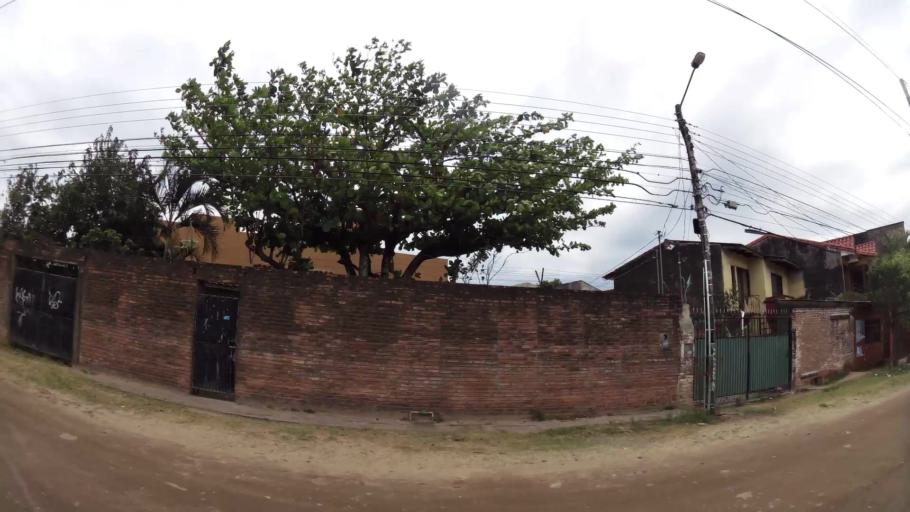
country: BO
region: Santa Cruz
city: Santa Cruz de la Sierra
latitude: -17.7483
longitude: -63.1850
